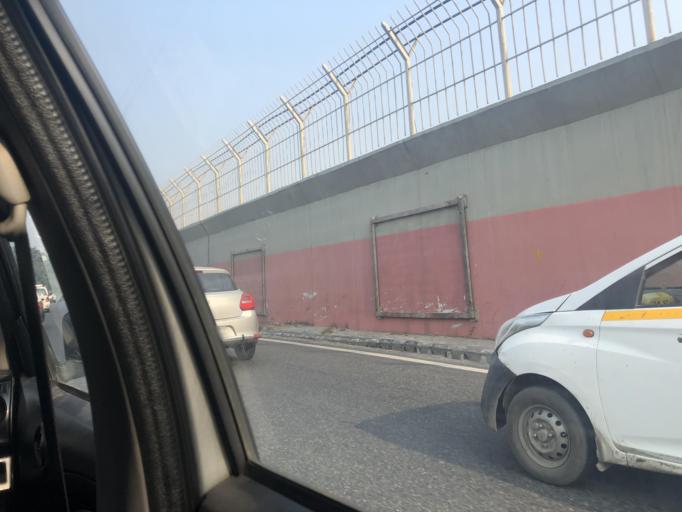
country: IN
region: NCT
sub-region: Central Delhi
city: Karol Bagh
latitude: 28.6131
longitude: 77.1368
